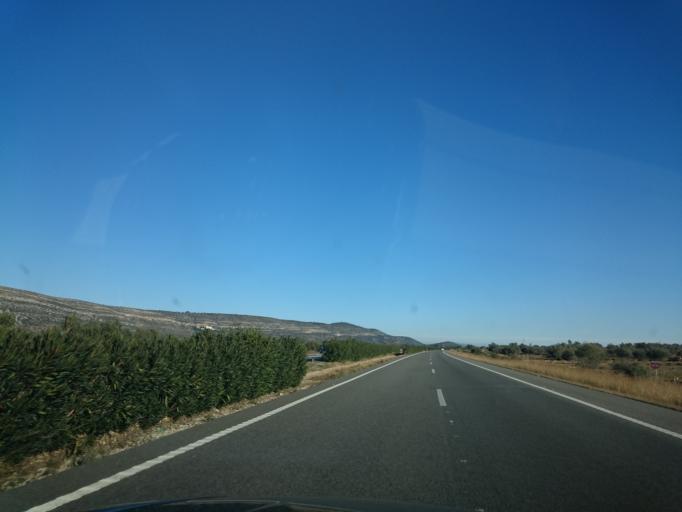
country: ES
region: Catalonia
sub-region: Provincia de Tarragona
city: Ulldecona
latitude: 40.6051
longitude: 0.4741
